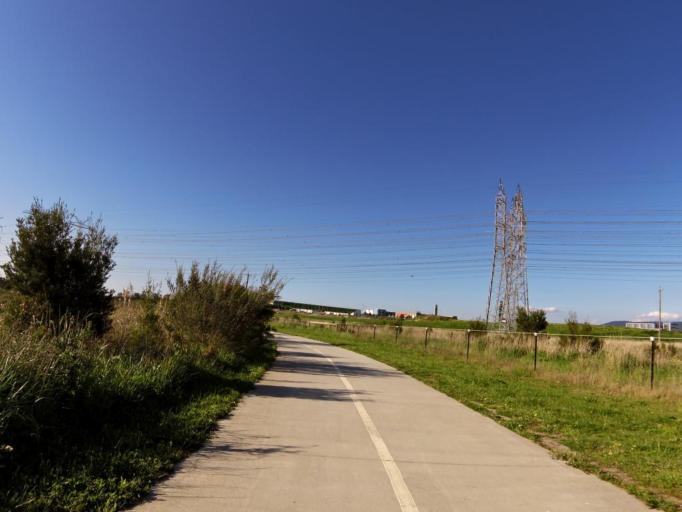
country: AU
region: Victoria
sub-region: Monash
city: Mulgrave
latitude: -37.9159
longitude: 145.2118
